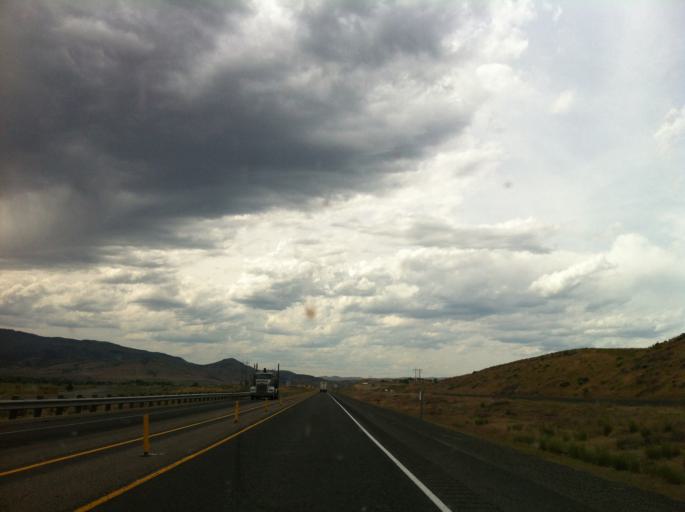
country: US
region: Oregon
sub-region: Baker County
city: Baker City
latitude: 44.5581
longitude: -117.4274
